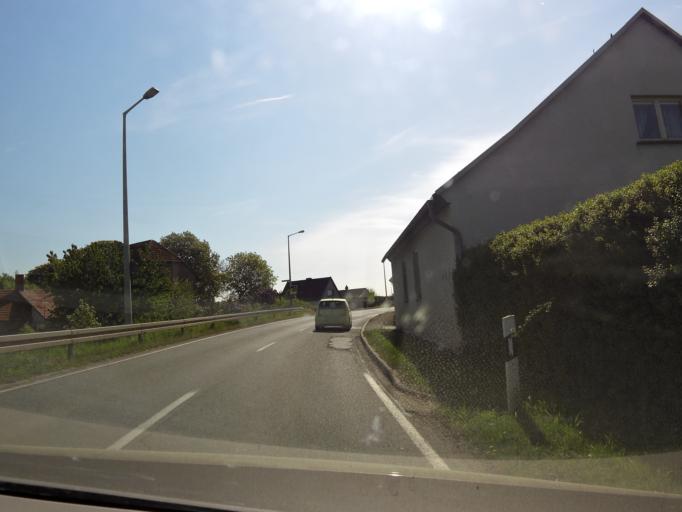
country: DE
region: Thuringia
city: Elxleben
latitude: 51.0336
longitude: 10.9673
